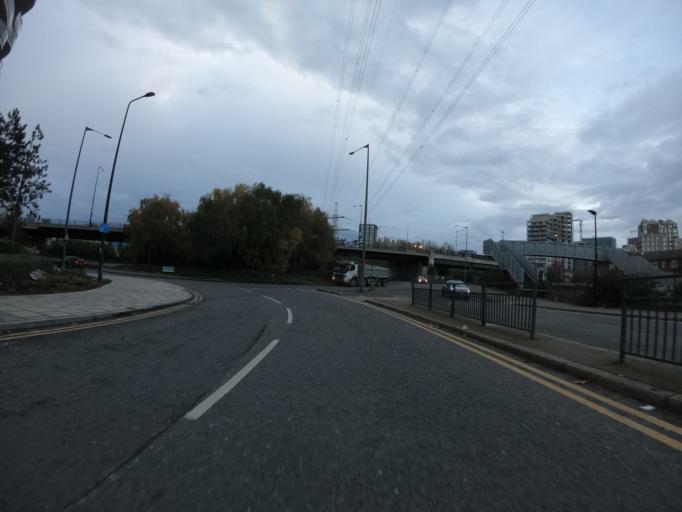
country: GB
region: England
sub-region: Greater London
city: Poplar
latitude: 51.5087
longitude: 0.0149
